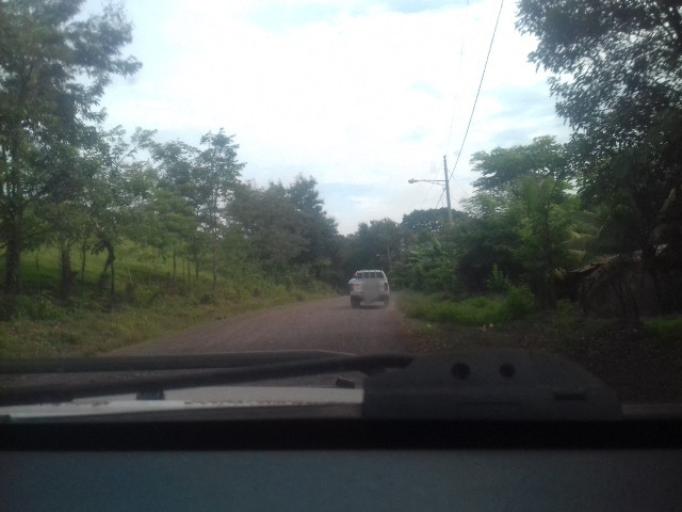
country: NI
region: Atlantico Norte (RAAN)
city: Waslala
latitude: 13.4086
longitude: -85.3198
